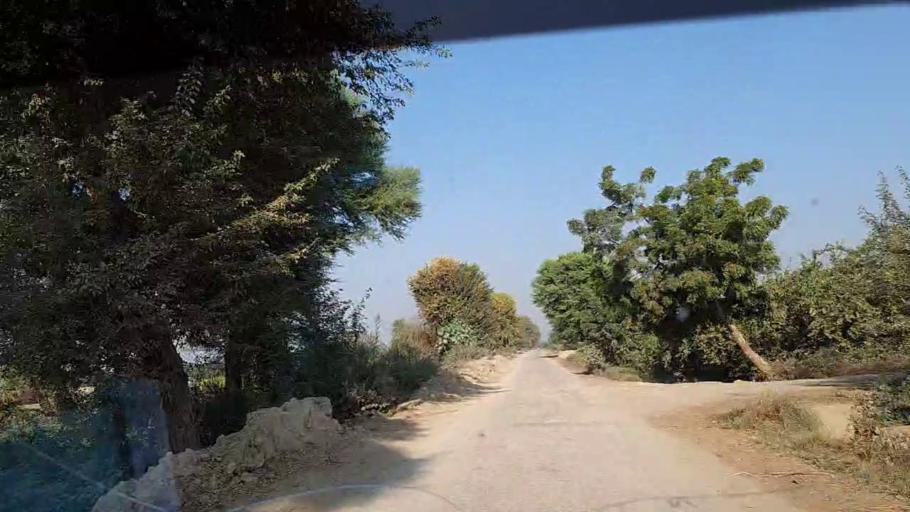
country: PK
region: Sindh
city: Sobhadero
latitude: 27.2468
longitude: 68.3256
